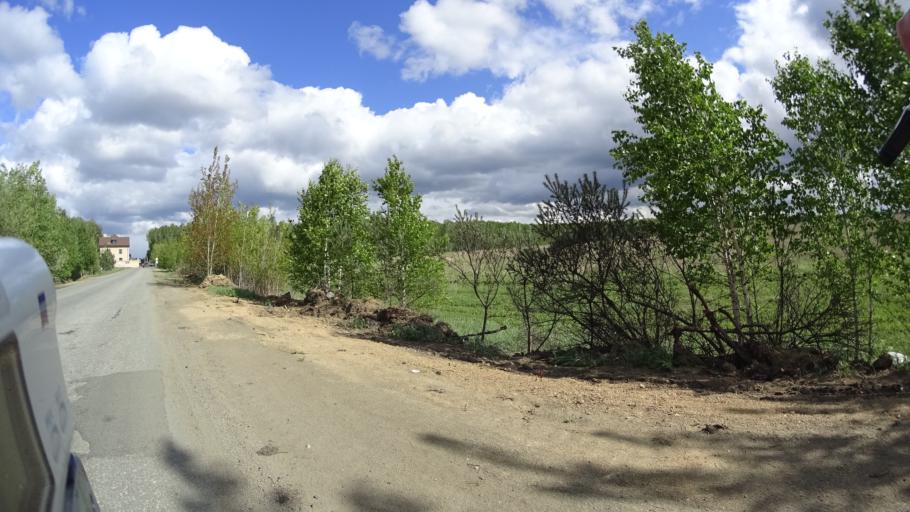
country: RU
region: Chelyabinsk
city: Sargazy
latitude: 55.1425
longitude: 61.2276
